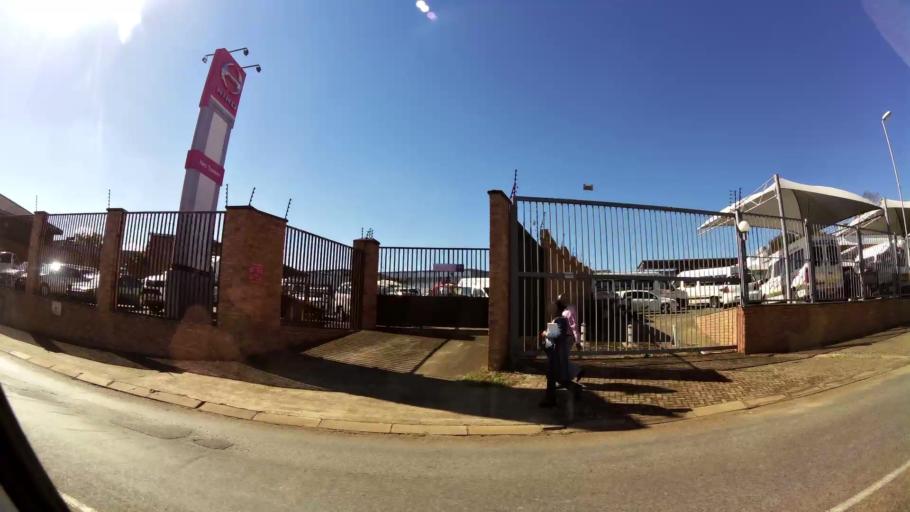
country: ZA
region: Limpopo
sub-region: Mopani District Municipality
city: Tzaneen
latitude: -23.8275
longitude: 30.1575
